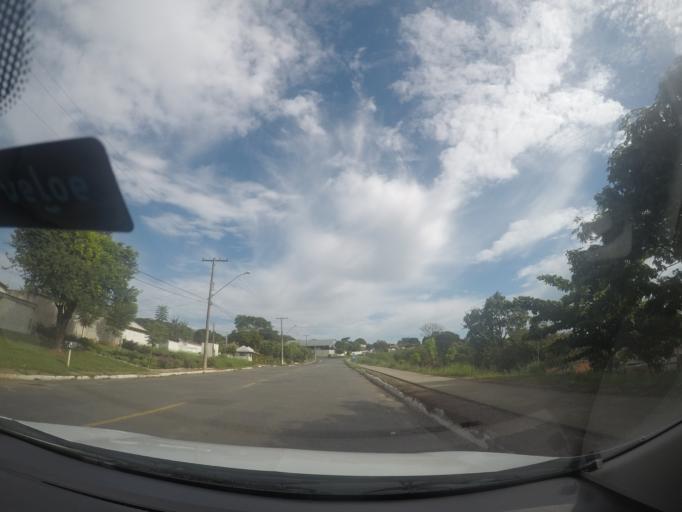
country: BR
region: Goias
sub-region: Goiania
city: Goiania
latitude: -16.6933
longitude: -49.2033
